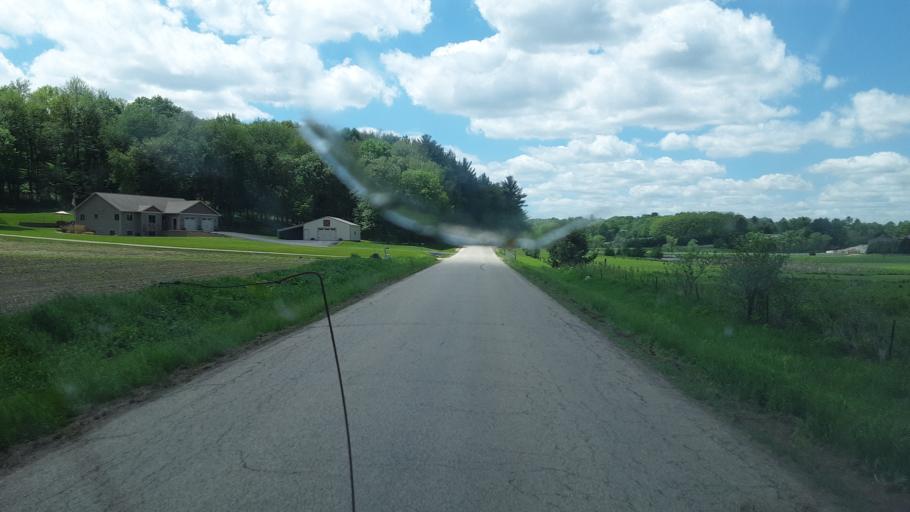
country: US
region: Wisconsin
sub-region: Sauk County
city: Reedsburg
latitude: 43.5766
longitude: -90.0369
